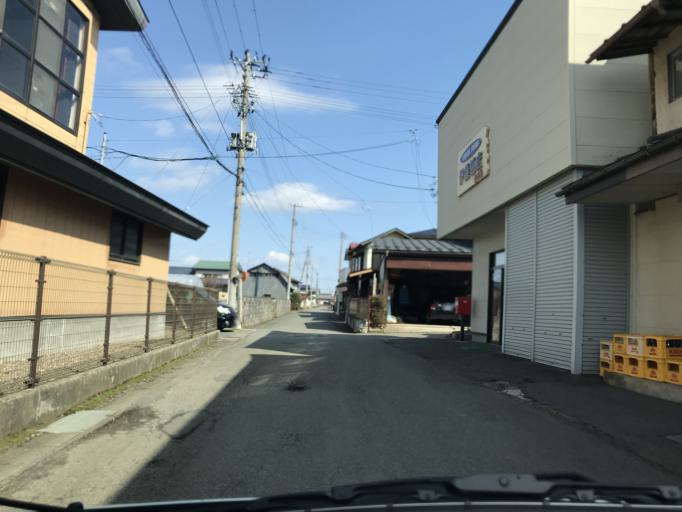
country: JP
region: Iwate
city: Mizusawa
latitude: 39.0467
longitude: 141.1449
